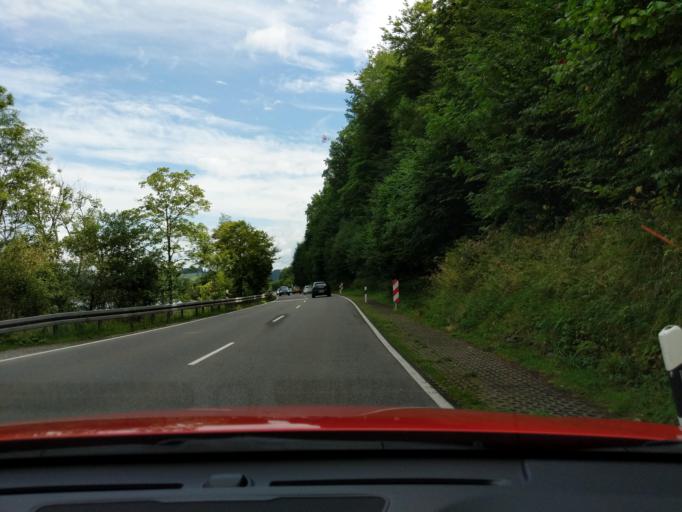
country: DE
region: Bavaria
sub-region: Swabia
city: Immenstadt im Allgau
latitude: 47.5669
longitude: 10.1643
